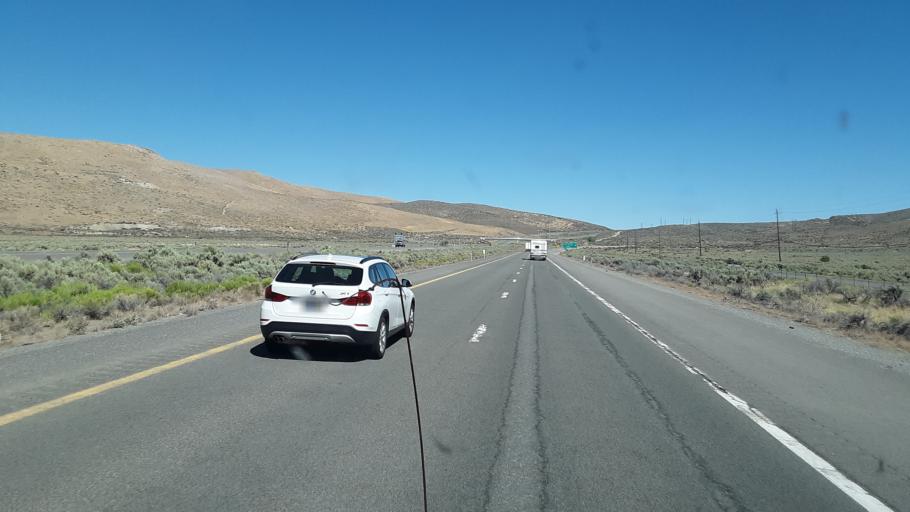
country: US
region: Nevada
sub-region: Washoe County
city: Cold Springs
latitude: 39.6471
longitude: -119.9681
